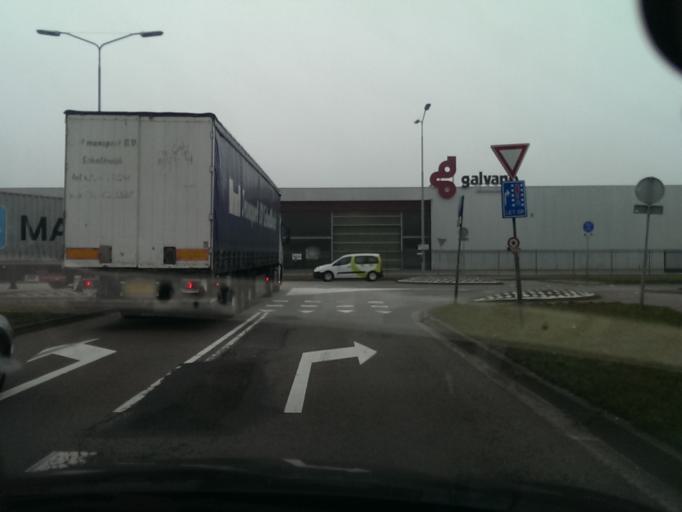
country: NL
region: North Brabant
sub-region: Gemeente Eindhoven
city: Meerhoven
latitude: 51.4667
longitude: 5.4192
